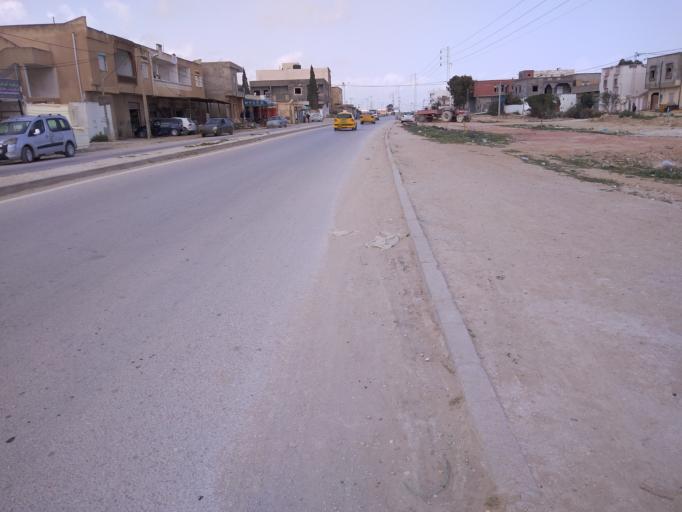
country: TN
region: Ariana
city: Ariana
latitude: 36.9486
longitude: 10.1733
